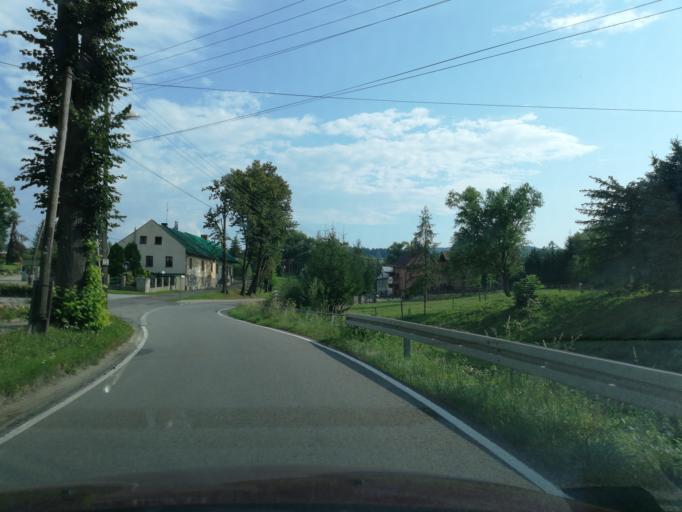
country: PL
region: Lesser Poland Voivodeship
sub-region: Powiat nowosadecki
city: Nawojowa
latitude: 49.5561
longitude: 20.7451
